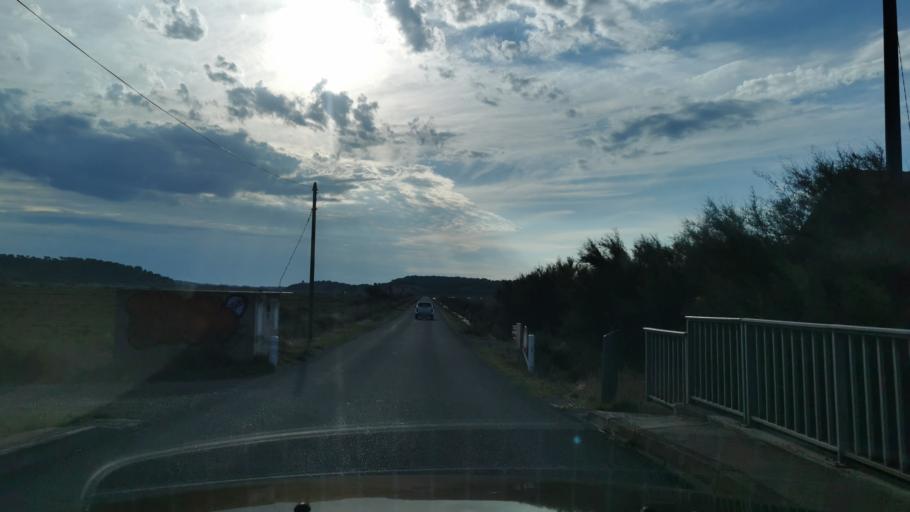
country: FR
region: Languedoc-Roussillon
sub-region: Departement de l'Aude
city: Gruissan
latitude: 43.1128
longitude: 3.0464
